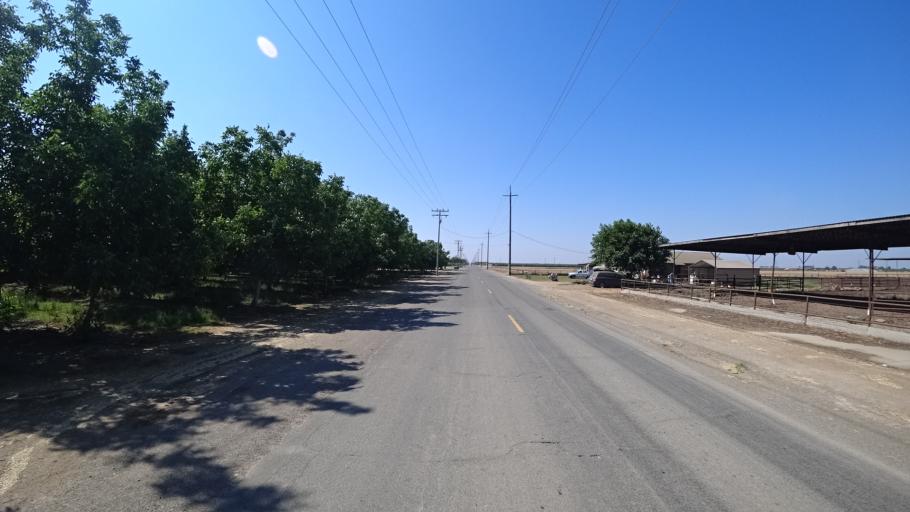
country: US
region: California
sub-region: Kings County
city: Hanford
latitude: 36.3662
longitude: -119.5830
